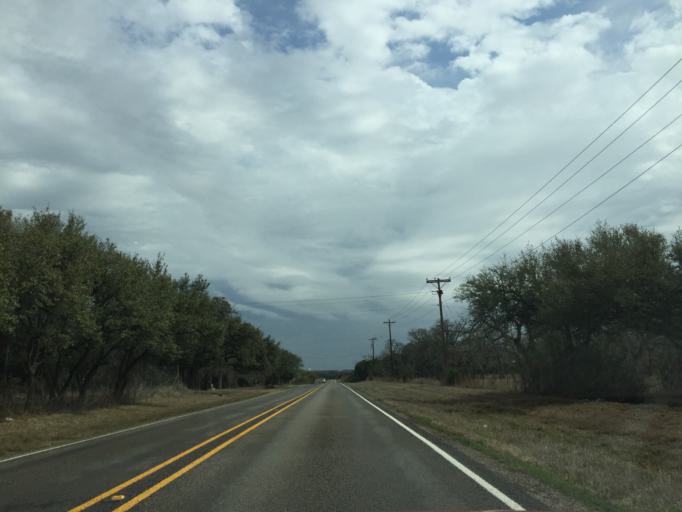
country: US
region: Texas
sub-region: Burnet County
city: Bertram
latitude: 30.6574
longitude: -97.9581
